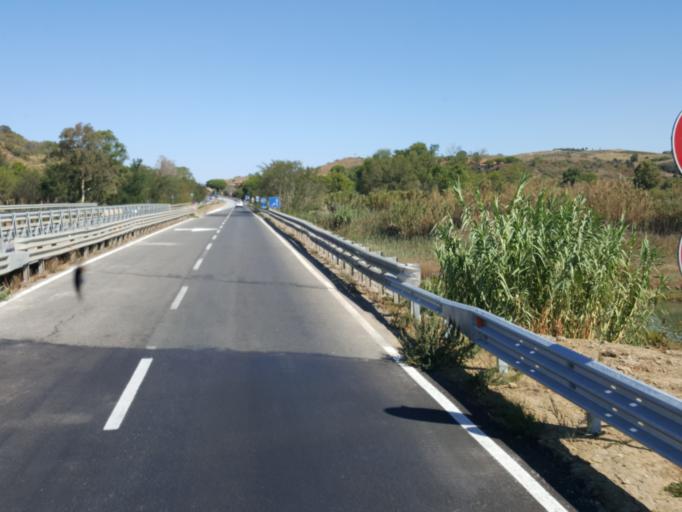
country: IT
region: Tuscany
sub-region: Provincia di Grosseto
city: Fonteblanda
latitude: 42.5482
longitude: 11.1747
